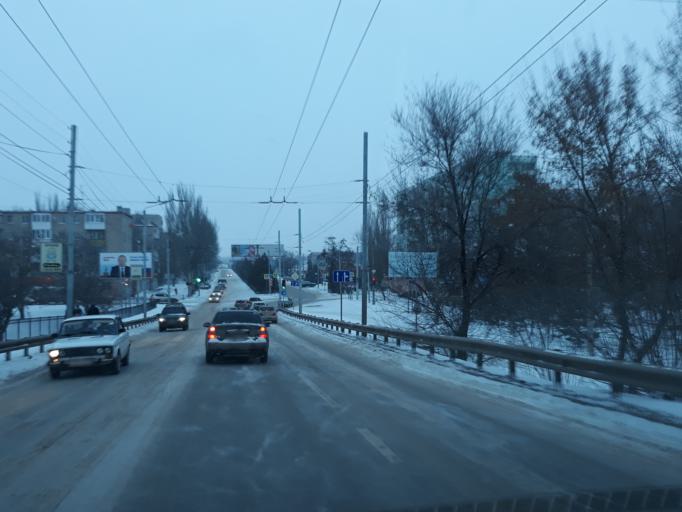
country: RU
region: Rostov
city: Taganrog
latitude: 47.2665
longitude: 38.9242
